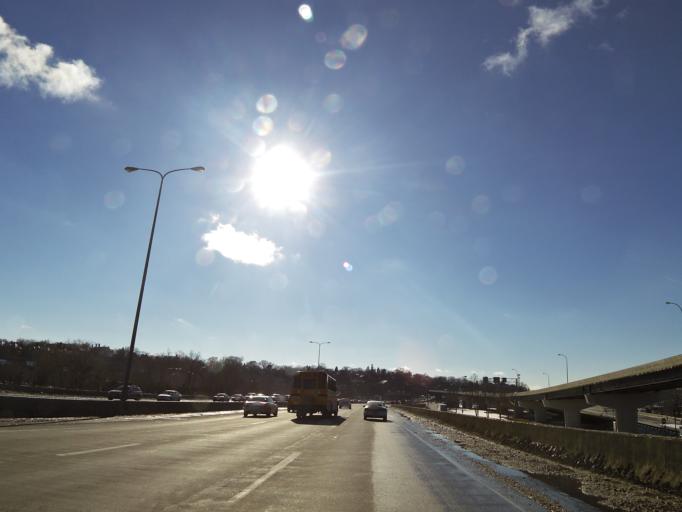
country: US
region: Minnesota
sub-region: Hennepin County
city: Minneapolis
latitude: 44.9734
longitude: -93.2938
